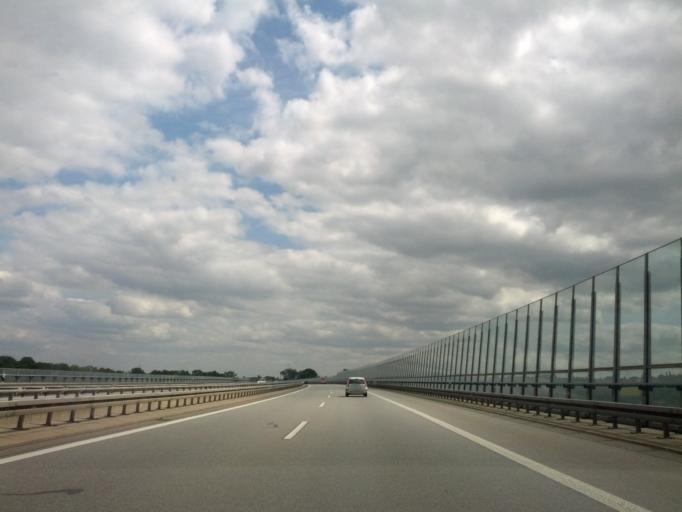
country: DE
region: Saxony
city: Kreischa
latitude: 50.9809
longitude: 13.7911
